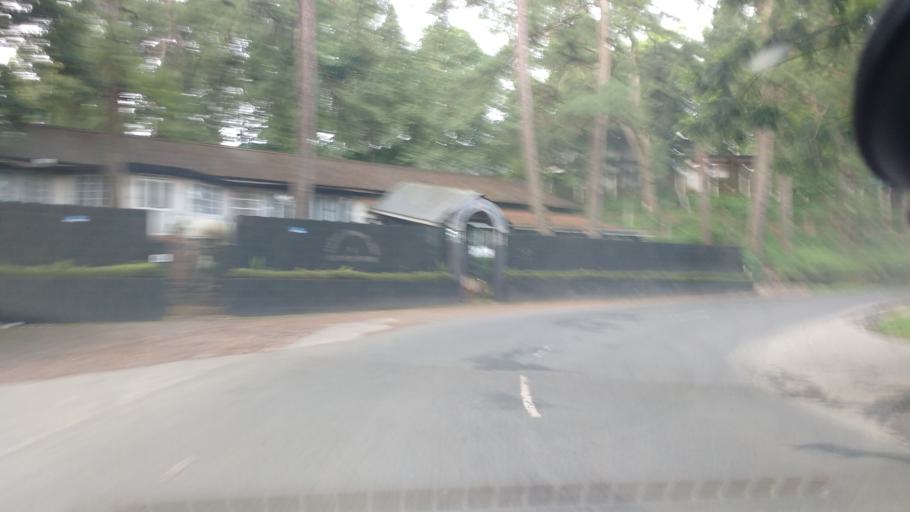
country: IN
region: Meghalaya
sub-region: East Khasi Hills
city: Shillong
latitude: 25.5704
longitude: 91.8657
